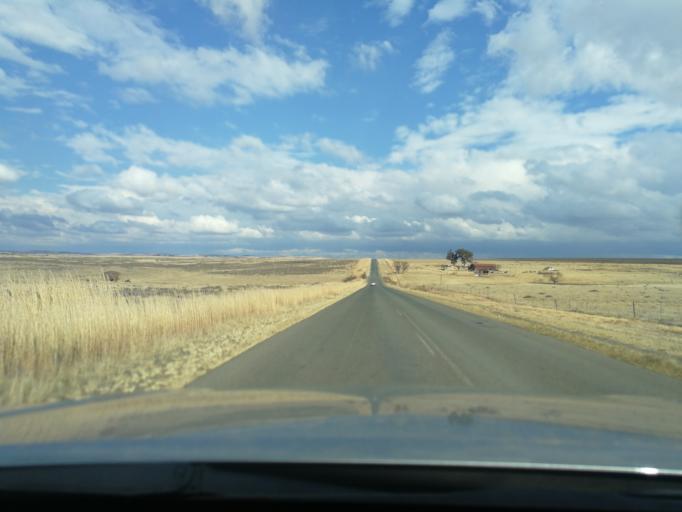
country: ZA
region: Orange Free State
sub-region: Fezile Dabi District Municipality
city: Frankfort
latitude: -27.4448
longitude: 28.5152
